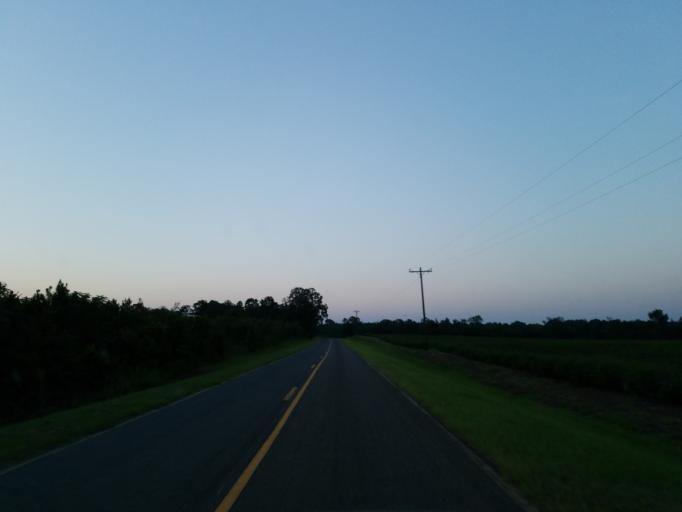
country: US
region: Georgia
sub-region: Dooly County
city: Unadilla
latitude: 32.2235
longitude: -83.7961
